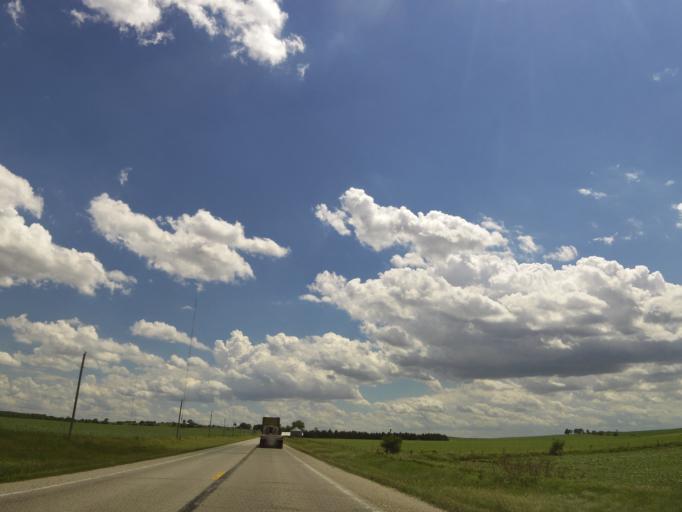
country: US
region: Iowa
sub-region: Benton County
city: Urbana
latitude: 42.3097
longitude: -91.8894
